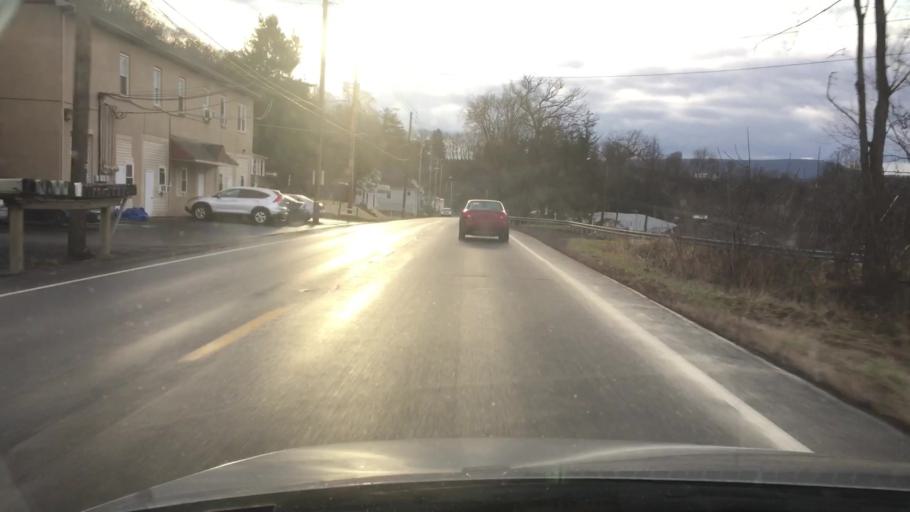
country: US
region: Pennsylvania
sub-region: Columbia County
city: Bloomsburg
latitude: 41.0093
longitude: -76.4637
